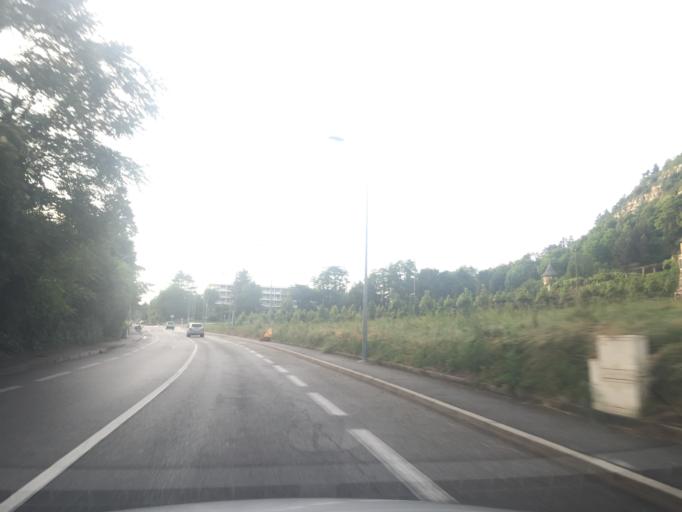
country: FR
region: Rhone-Alpes
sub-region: Departement de la Savoie
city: Bassens
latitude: 45.5841
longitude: 5.9242
